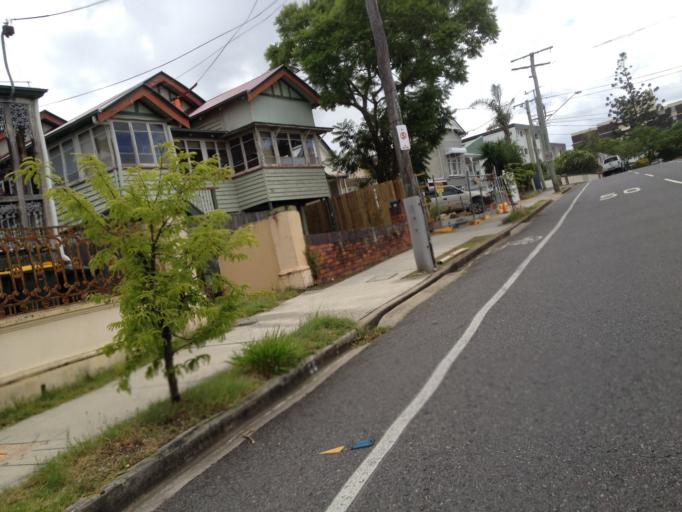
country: AU
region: Queensland
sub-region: Brisbane
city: South Brisbane
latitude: -27.4868
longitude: 153.0101
